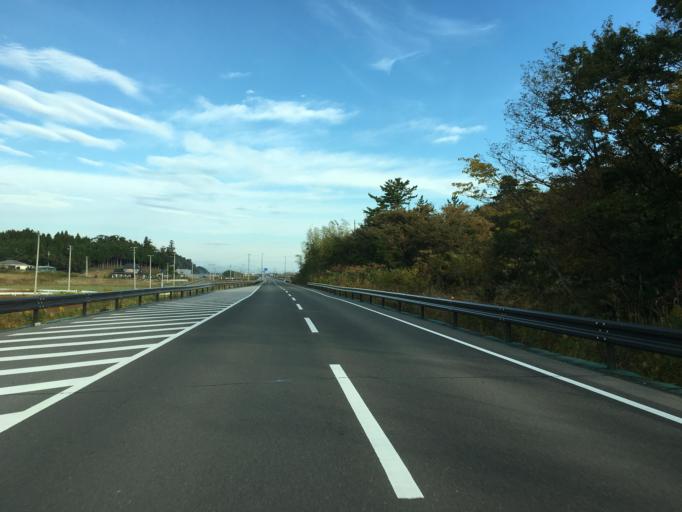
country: JP
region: Miyagi
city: Watari
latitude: 37.8958
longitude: 140.9246
